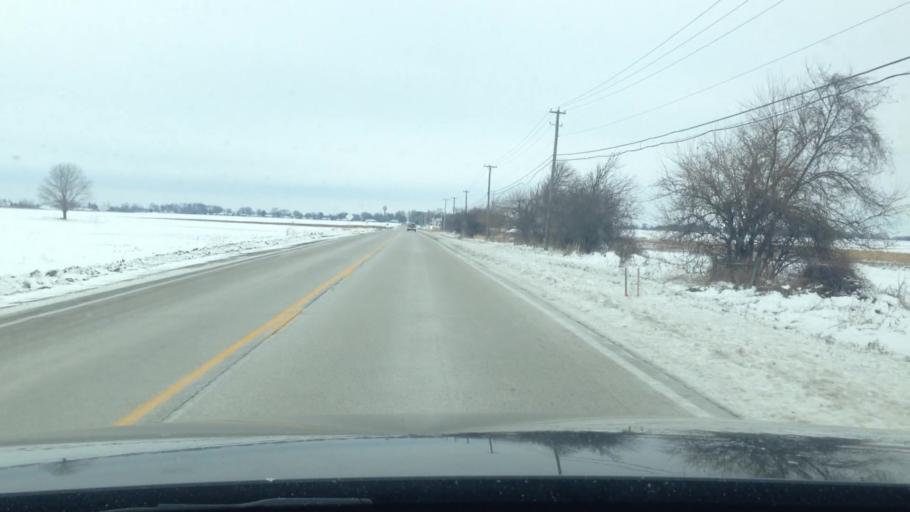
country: US
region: Illinois
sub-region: McHenry County
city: Hebron
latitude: 42.4468
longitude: -88.4330
